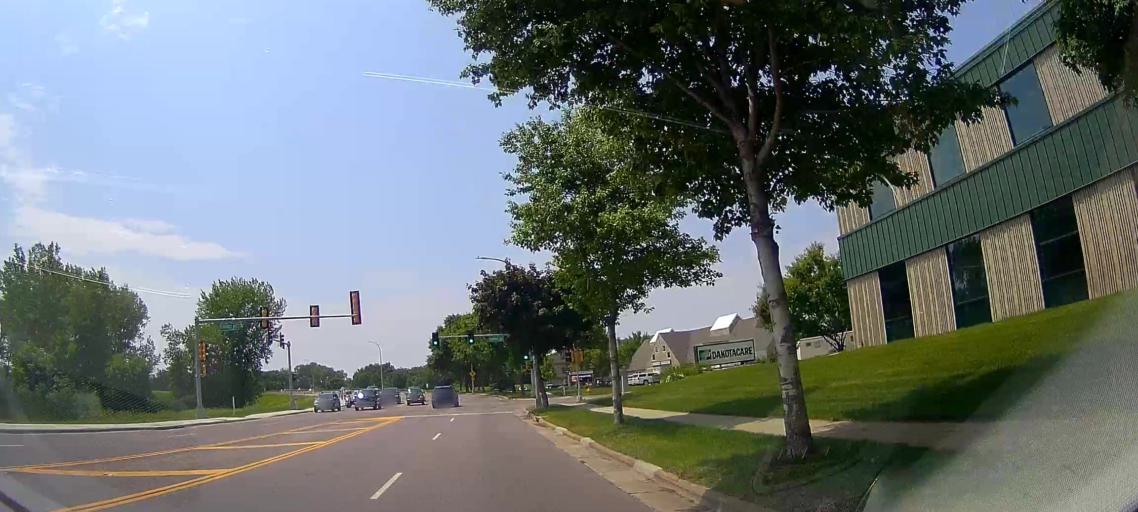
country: US
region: South Dakota
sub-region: Minnehaha County
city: Sioux Falls
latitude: 43.5085
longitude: -96.7576
